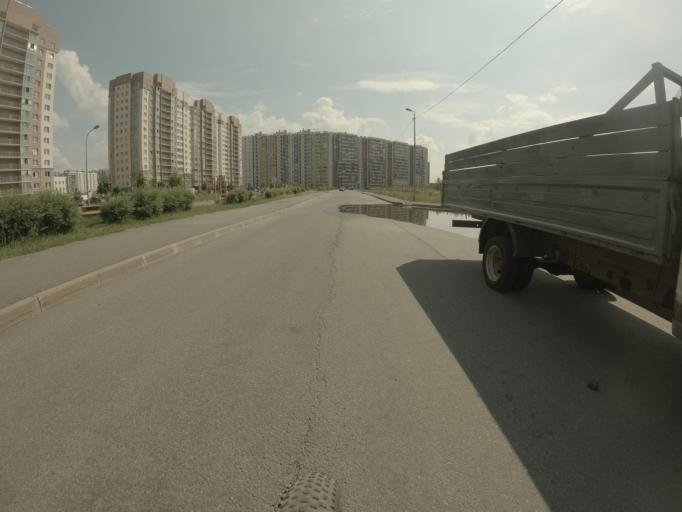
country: RU
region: St.-Petersburg
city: Krasnogvargeisky
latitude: 59.9186
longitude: 30.4380
